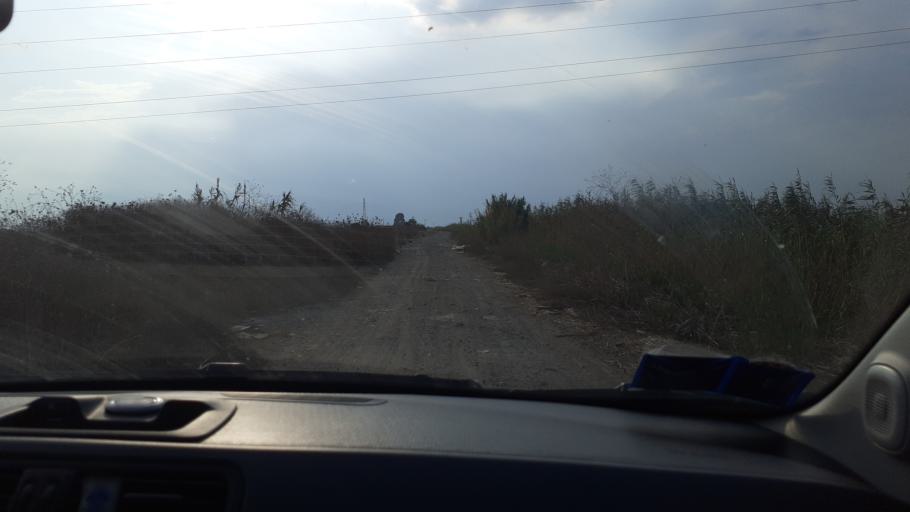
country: IT
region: Sicily
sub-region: Catania
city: Catania
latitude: 37.4330
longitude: 15.0120
